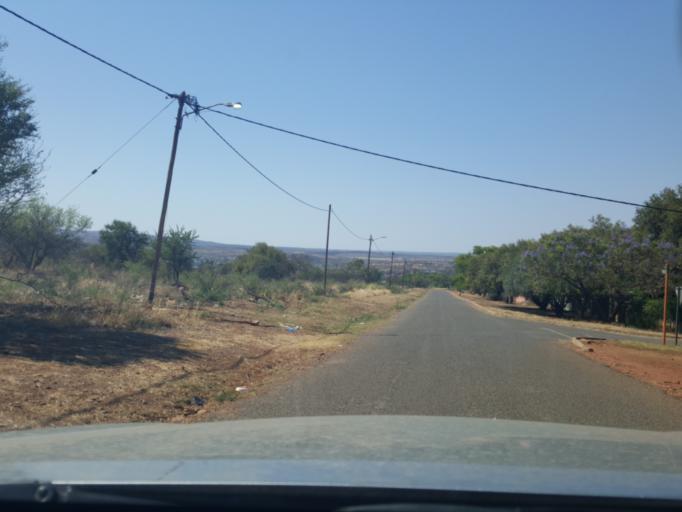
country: ZA
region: North-West
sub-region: Ngaka Modiri Molema District Municipality
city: Zeerust
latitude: -25.5331
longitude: 26.0817
